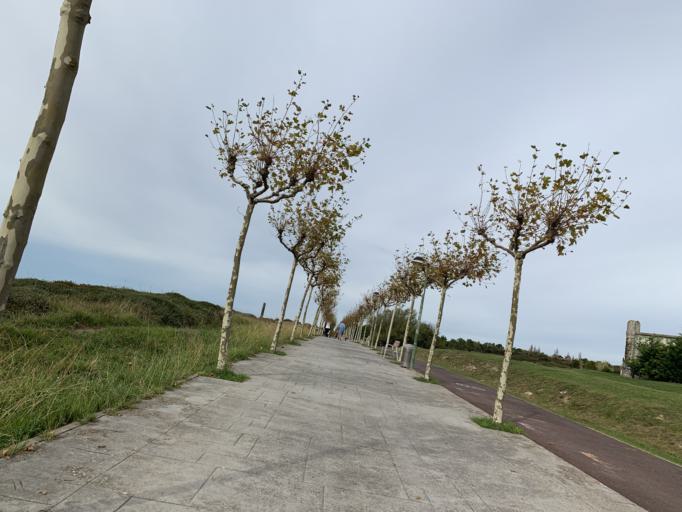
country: ES
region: Basque Country
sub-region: Bizkaia
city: Getxo
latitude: 43.3622
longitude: -3.0235
